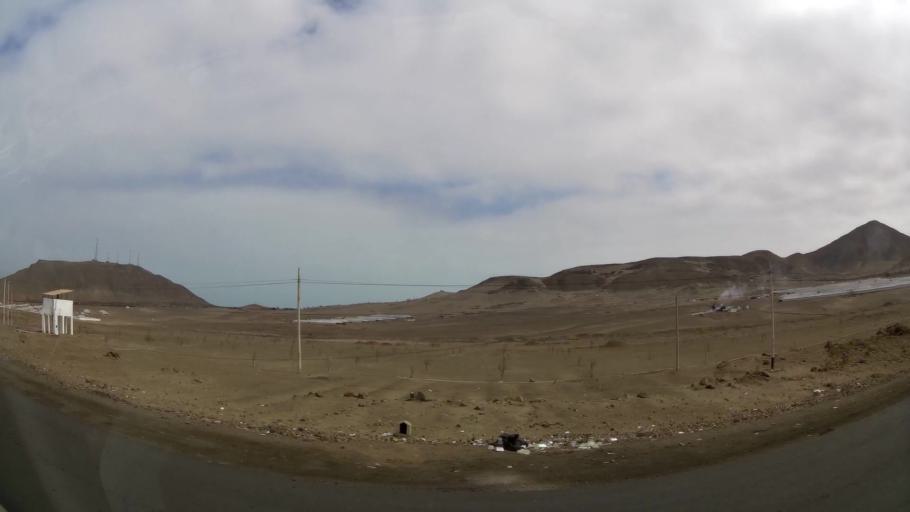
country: PE
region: Lima
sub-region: Provincia de Canete
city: Mala
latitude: -12.6086
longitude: -76.6657
